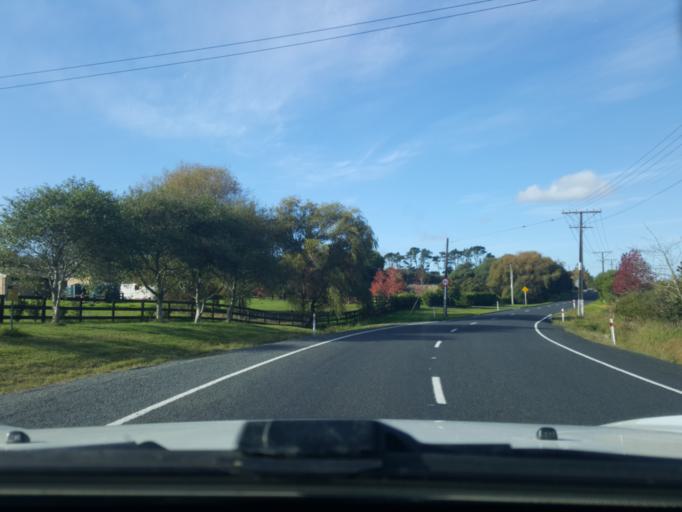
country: NZ
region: Auckland
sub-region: Auckland
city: Muriwai Beach
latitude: -36.7705
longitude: 174.5690
